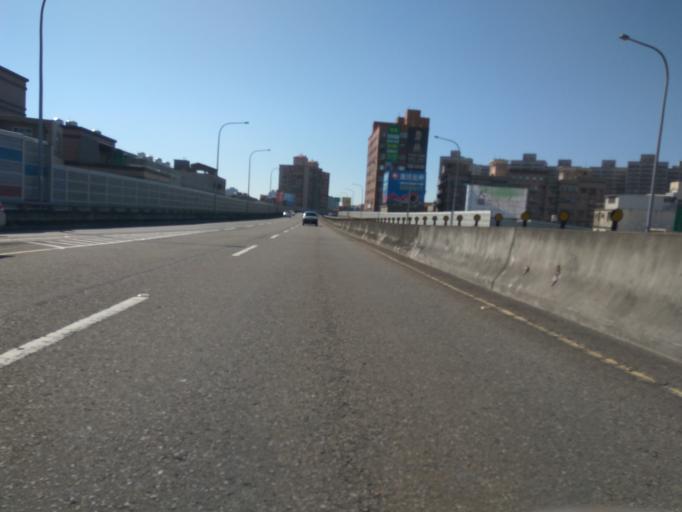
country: TW
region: Taiwan
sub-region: Hsinchu
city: Hsinchu
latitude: 24.8256
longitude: 120.9715
